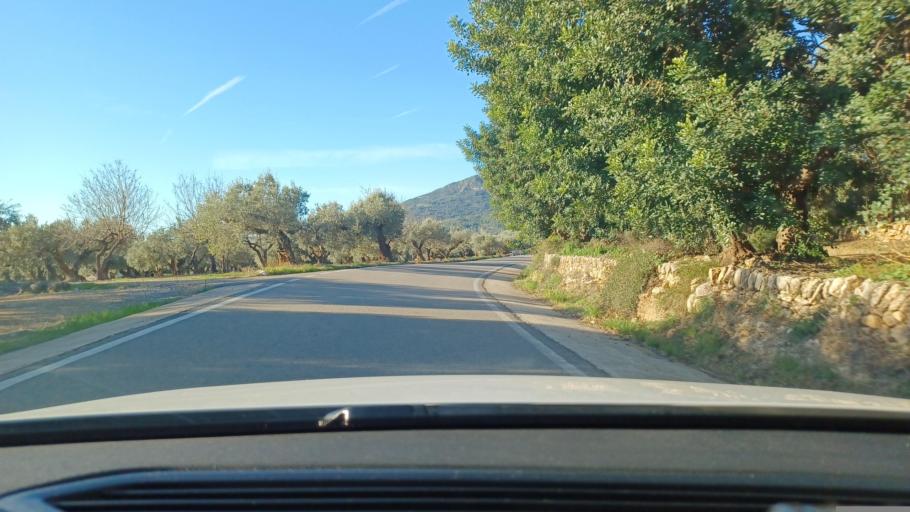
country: ES
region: Catalonia
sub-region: Provincia de Tarragona
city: Mas de Barberans
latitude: 40.7180
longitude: 0.3620
